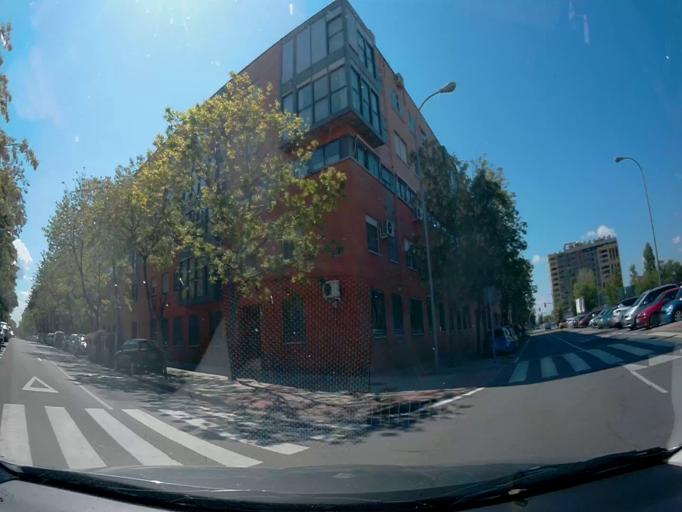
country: ES
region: Madrid
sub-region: Provincia de Madrid
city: Vicalvaro
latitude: 40.3997
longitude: -3.6241
